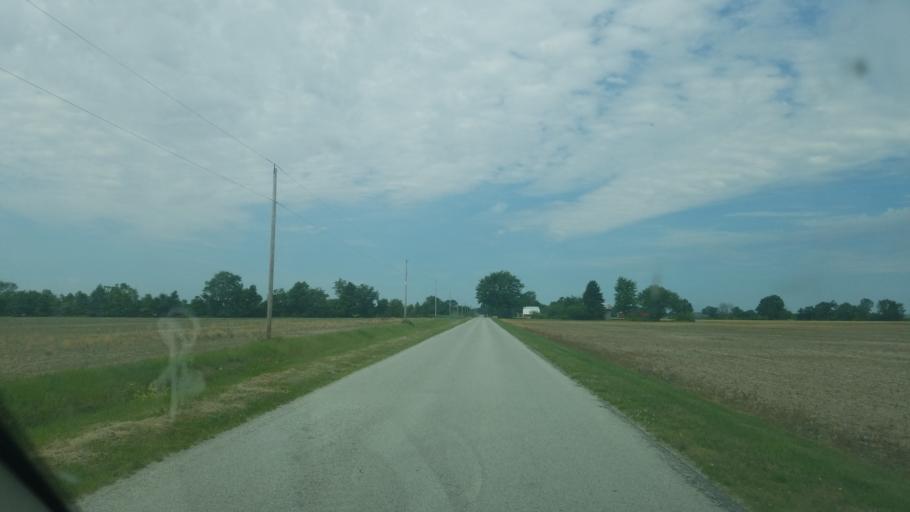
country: US
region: Ohio
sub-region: Wood County
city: North Baltimore
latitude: 41.2327
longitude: -83.5941
